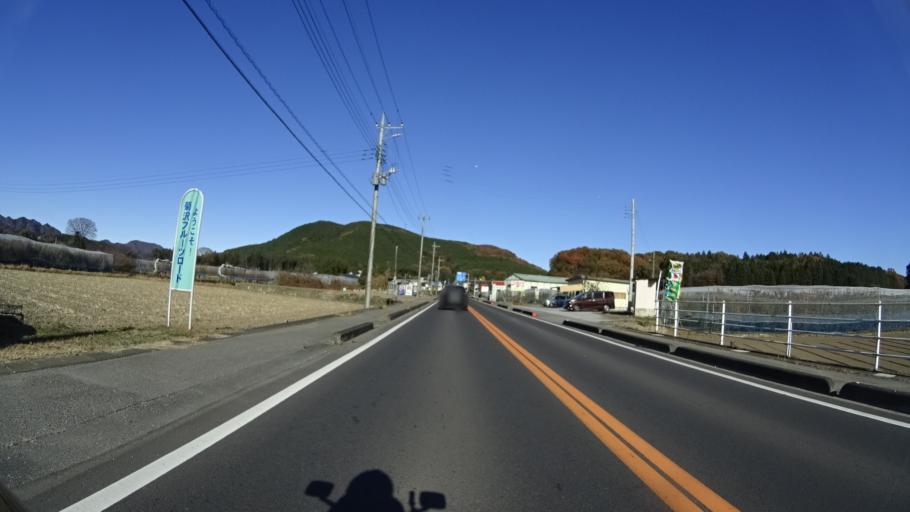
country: JP
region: Tochigi
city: Kanuma
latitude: 36.5922
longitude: 139.7971
